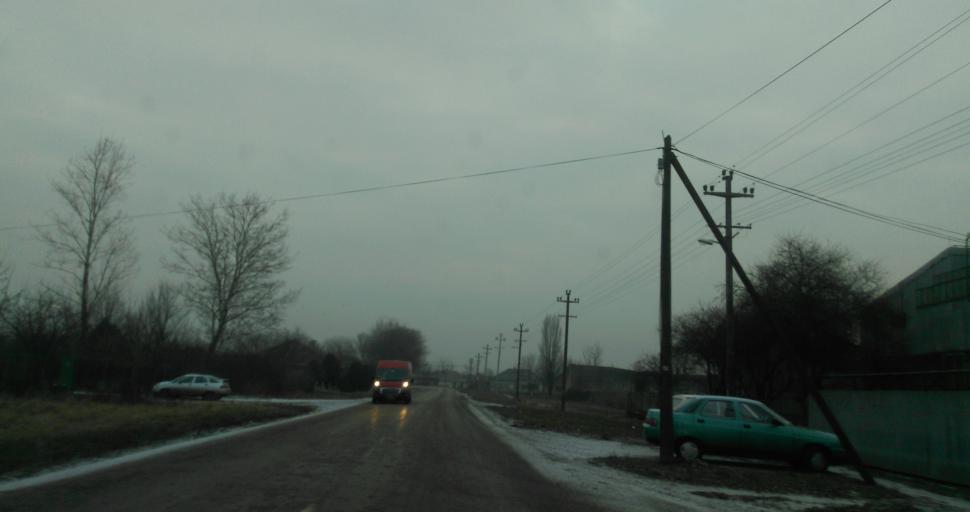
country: RS
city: Kumane
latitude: 45.5364
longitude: 20.2159
